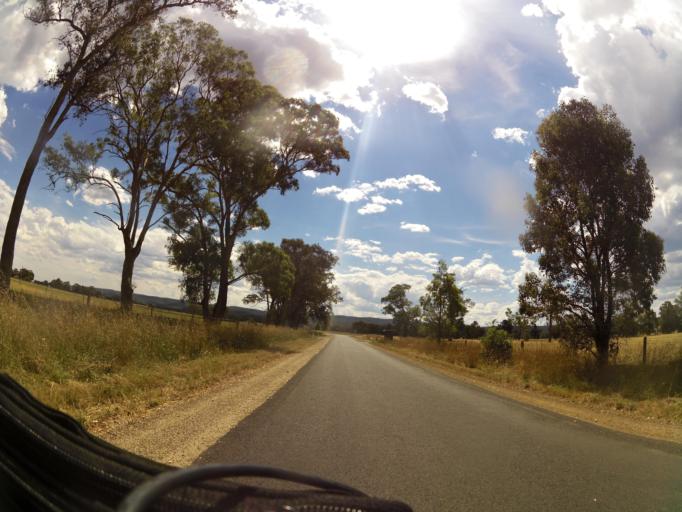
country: AU
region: Victoria
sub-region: Wellington
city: Heyfield
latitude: -37.9800
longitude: 146.6965
